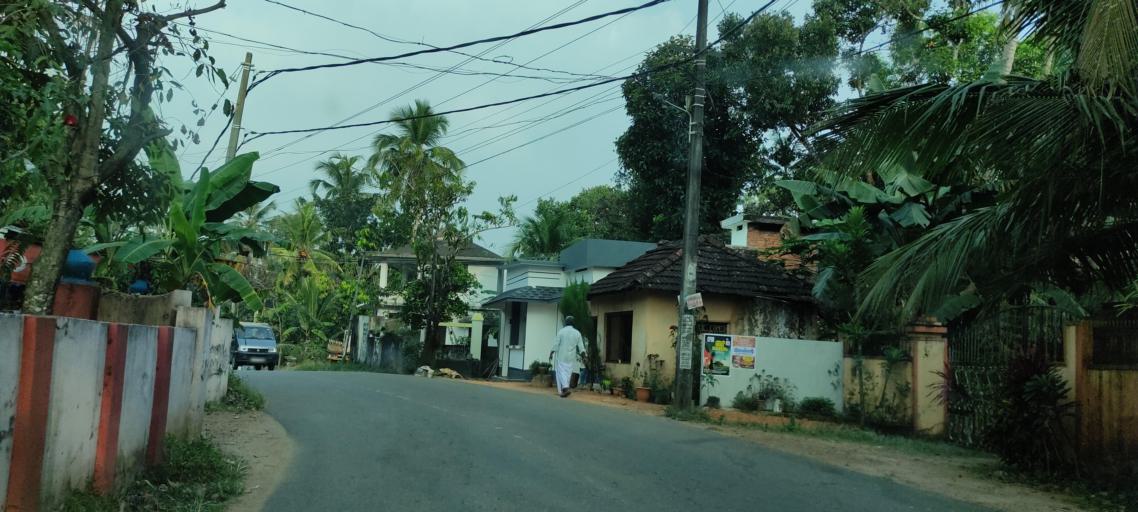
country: IN
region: Kerala
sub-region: Pattanamtitta
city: Adur
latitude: 9.0887
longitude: 76.7429
